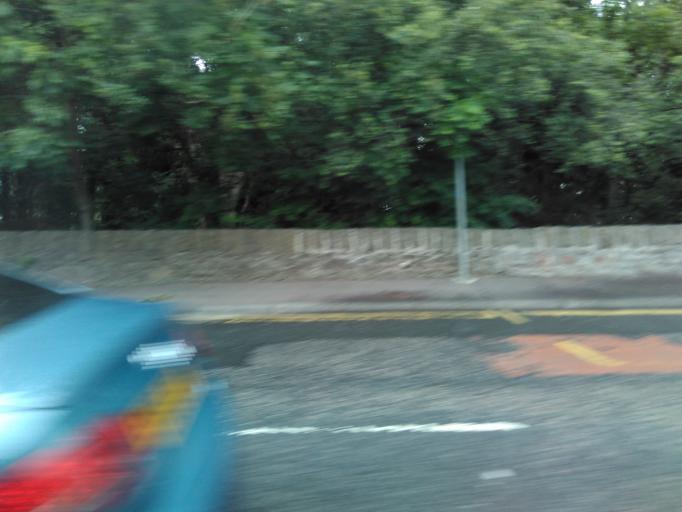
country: GB
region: Scotland
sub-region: Edinburgh
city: Edinburgh
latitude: 55.9241
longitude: -3.1662
